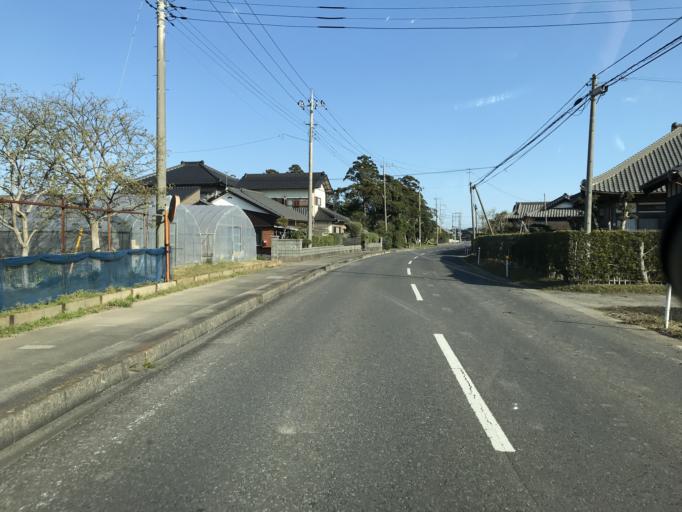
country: JP
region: Chiba
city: Omigawa
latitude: 35.8417
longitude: 140.6195
